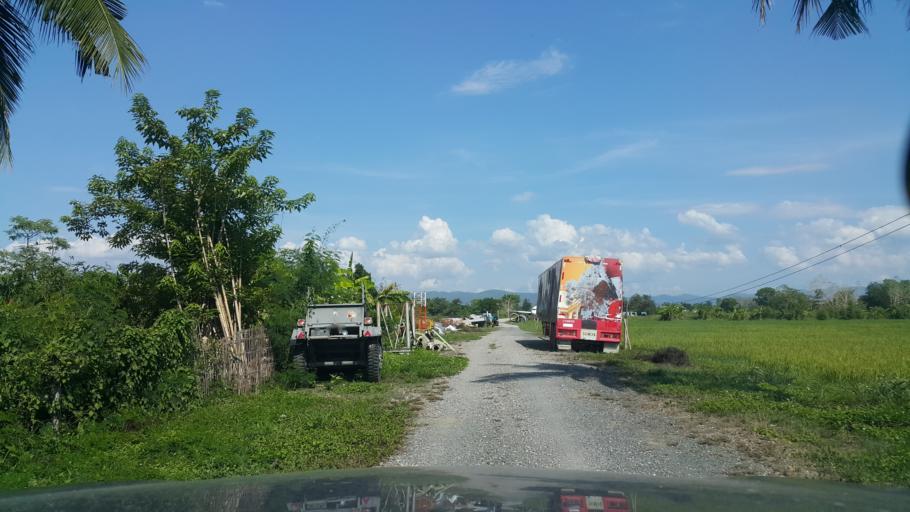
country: TH
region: Chiang Mai
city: San Kamphaeng
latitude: 18.8056
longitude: 99.1168
